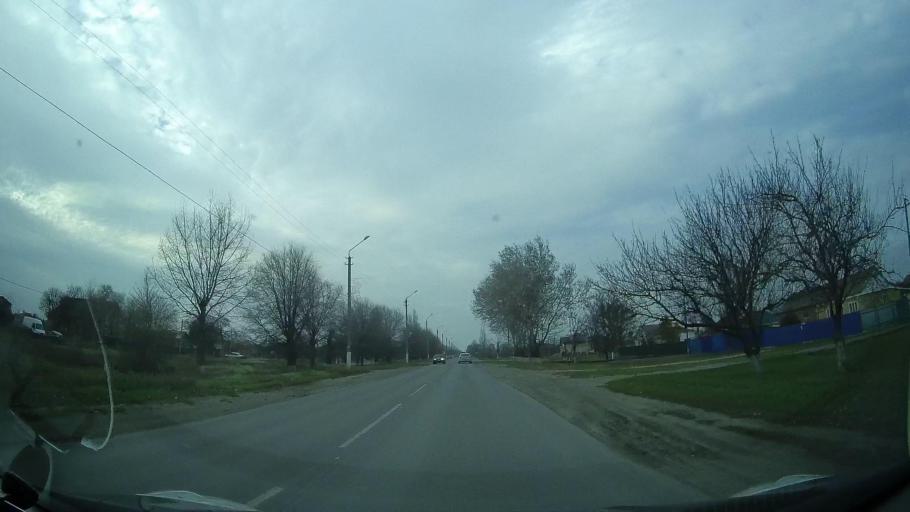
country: RU
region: Rostov
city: Ol'ginskaya
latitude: 47.1831
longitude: 39.9576
